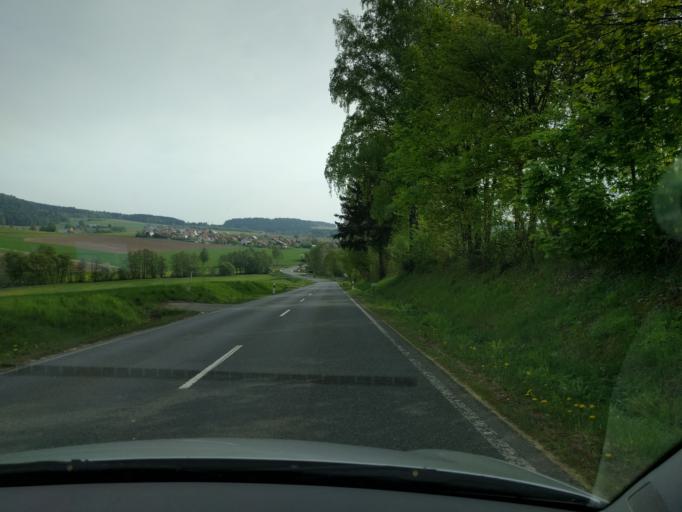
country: DE
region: Bavaria
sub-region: Upper Palatinate
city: Falkenstein
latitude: 49.1027
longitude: 12.4943
